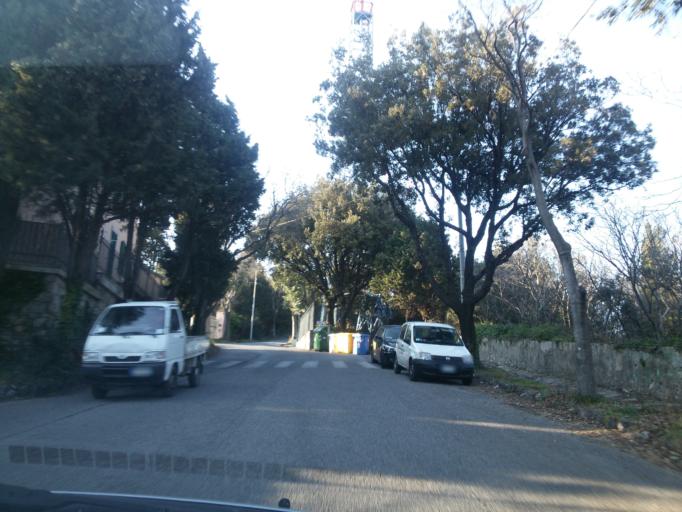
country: IT
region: Liguria
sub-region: Provincia di Genova
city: Genoa
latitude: 44.4189
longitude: 8.9418
